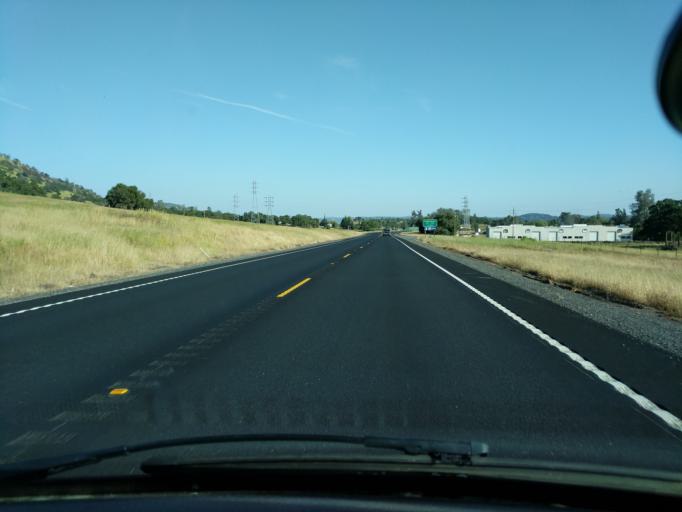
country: US
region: California
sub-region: Calaveras County
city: Copperopolis
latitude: 37.9876
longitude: -120.6478
